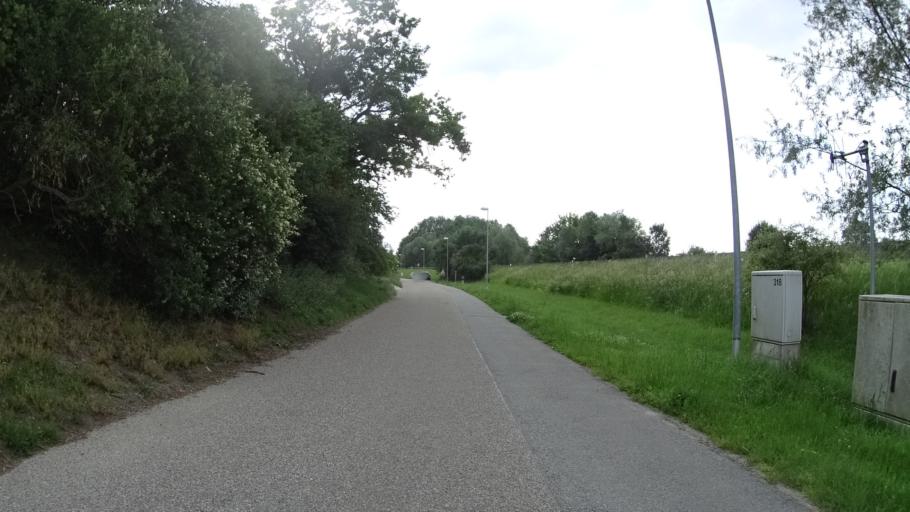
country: DE
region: Bavaria
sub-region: Lower Bavaria
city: Bogen
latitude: 48.8999
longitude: 12.6964
